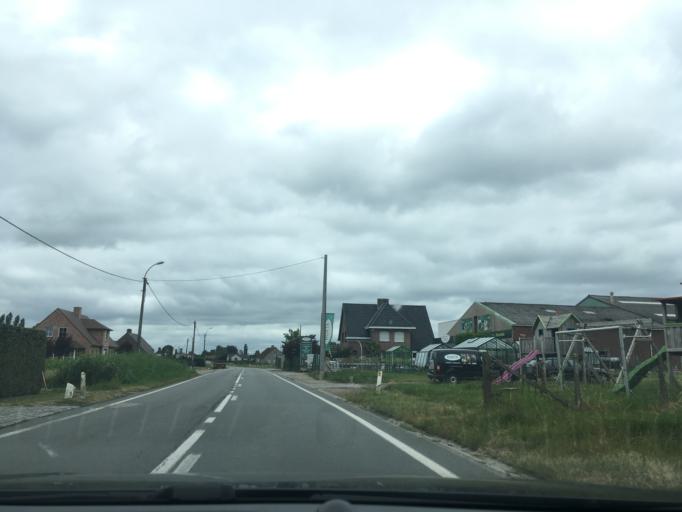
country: BE
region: Flanders
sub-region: Provincie West-Vlaanderen
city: Wingene
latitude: 51.0679
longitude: 3.2863
